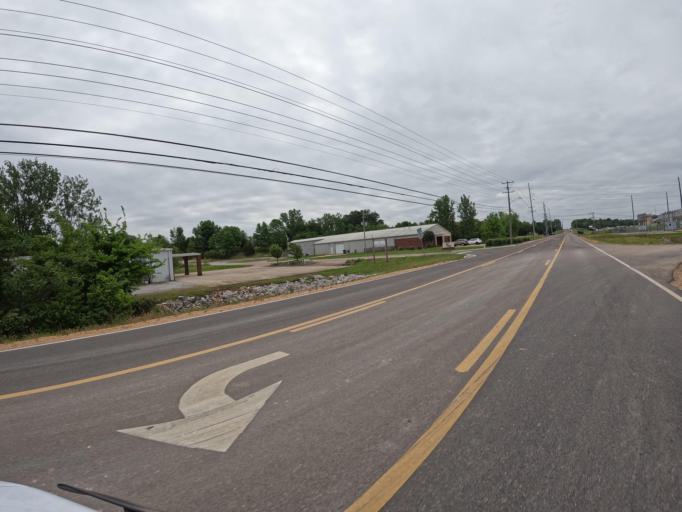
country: US
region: Mississippi
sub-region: Lee County
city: Tupelo
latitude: 34.2756
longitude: -88.7643
